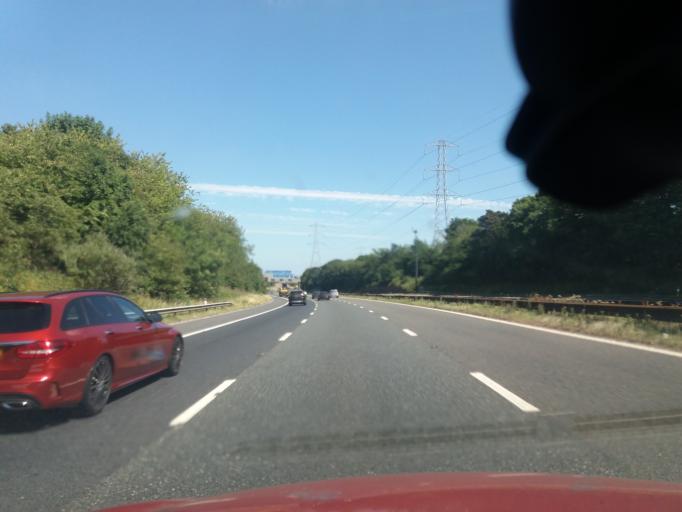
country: GB
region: England
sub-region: City and Borough of Salford
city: Little Hulton
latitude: 53.5387
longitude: -2.4096
